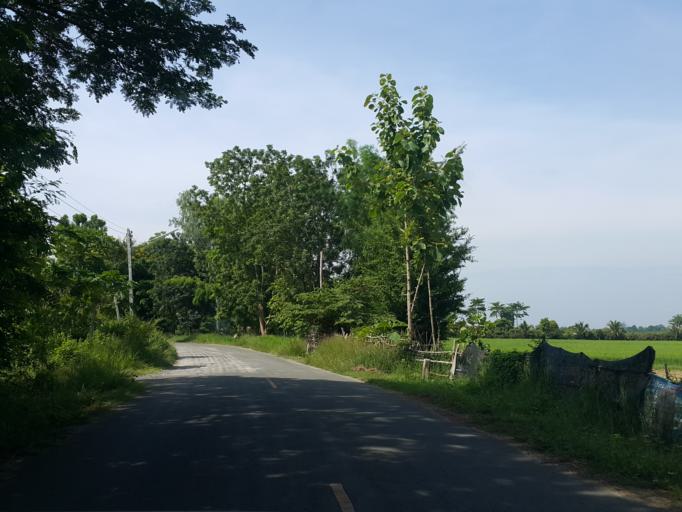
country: TH
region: Chiang Mai
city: San Kamphaeng
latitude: 18.7140
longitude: 99.0916
